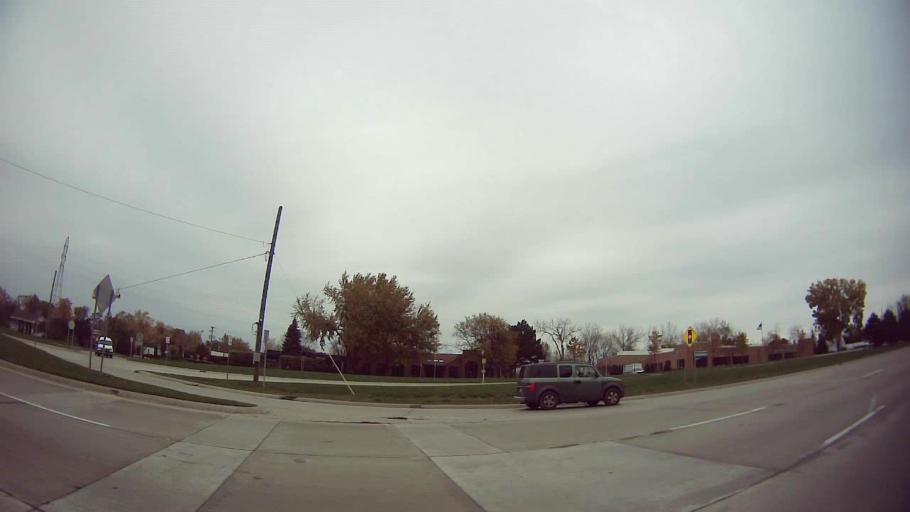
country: US
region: Michigan
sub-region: Oakland County
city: Sylvan Lake
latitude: 42.6167
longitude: -83.3163
